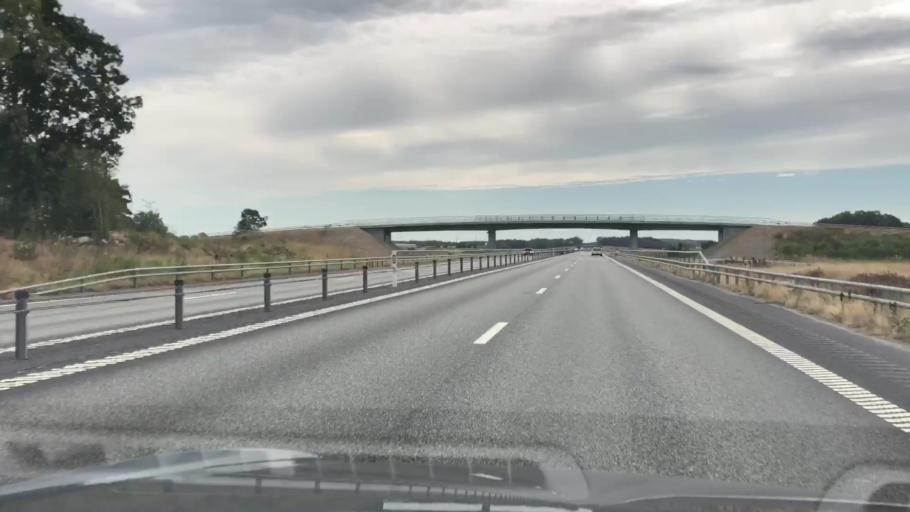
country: SE
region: Blekinge
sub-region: Karlshamns Kommun
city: Morrum
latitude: 56.1331
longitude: 14.6599
